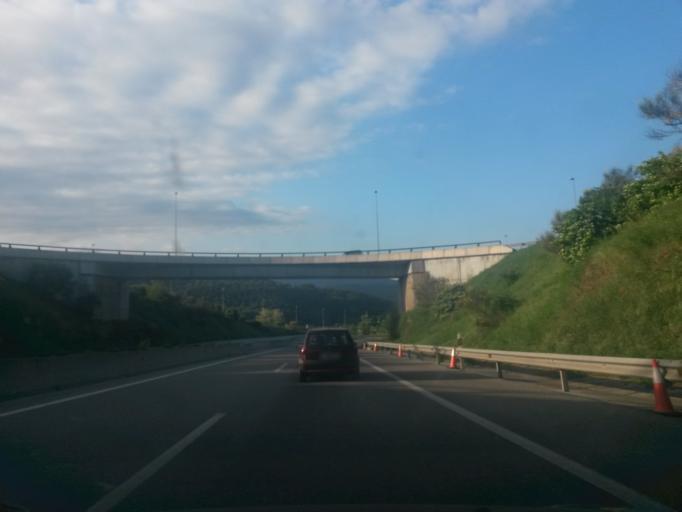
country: ES
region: Catalonia
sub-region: Provincia de Girona
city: Sant Joan les Fonts
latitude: 42.2097
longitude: 2.5390
